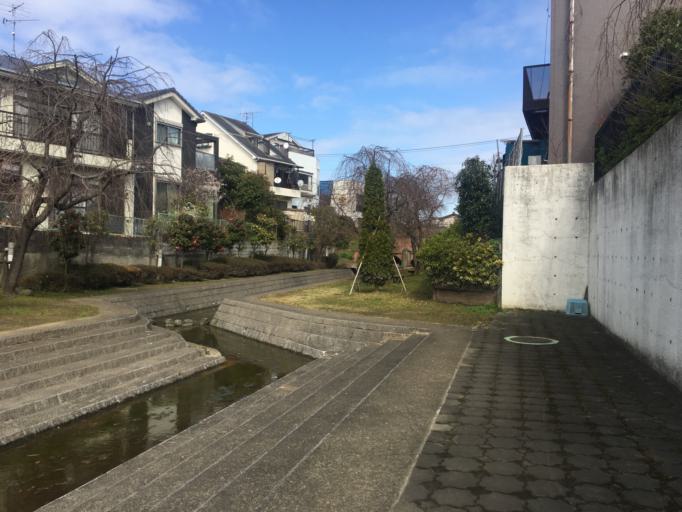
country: JP
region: Saitama
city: Shiki
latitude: 35.8631
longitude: 139.5969
